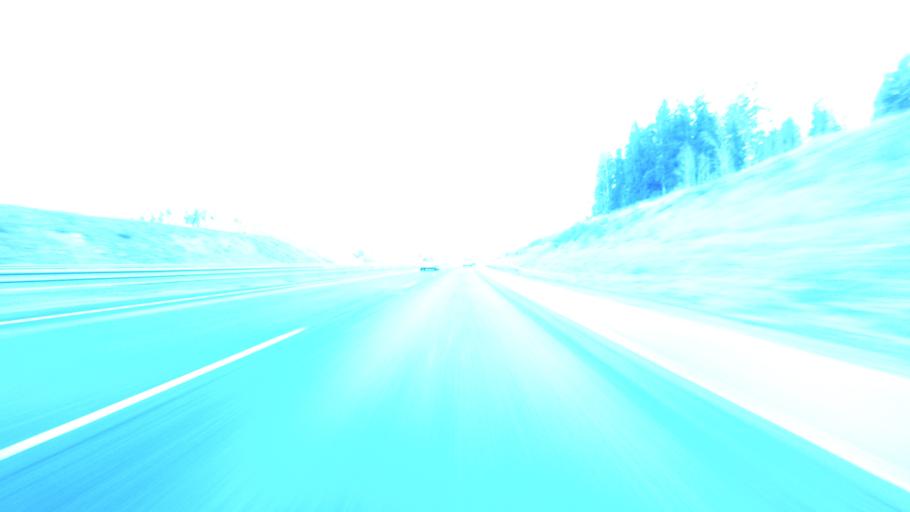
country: FI
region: Uusimaa
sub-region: Helsinki
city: Lohja
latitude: 60.3000
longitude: 24.0552
